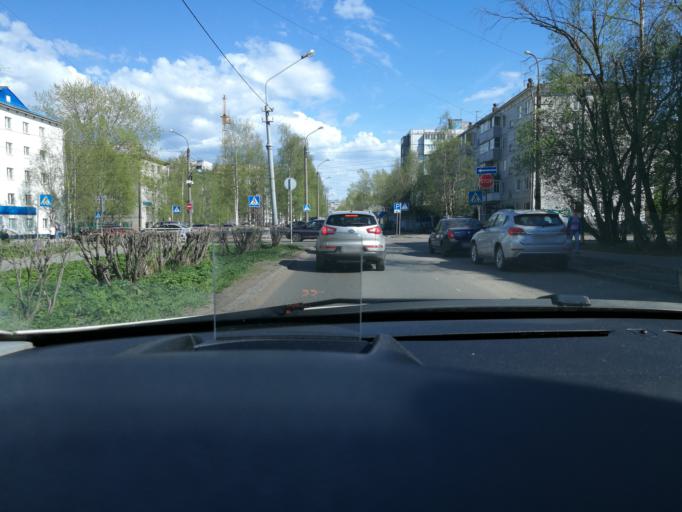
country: RU
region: Arkhangelskaya
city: Arkhangel'sk
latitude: 64.5479
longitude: 40.5335
